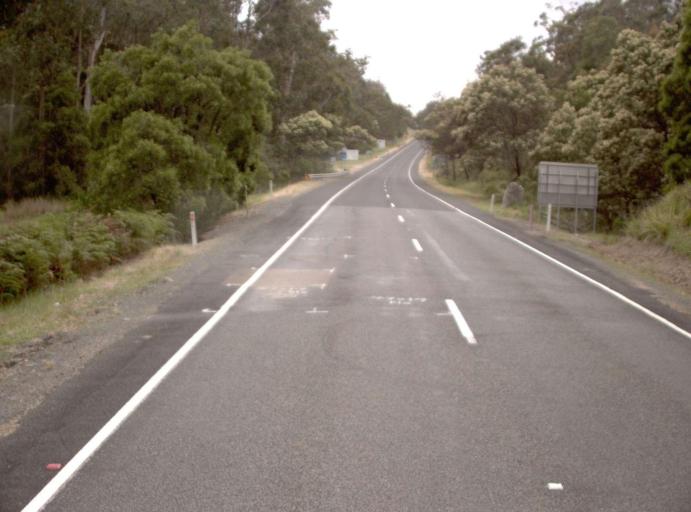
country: AU
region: New South Wales
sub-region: Bombala
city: Bombala
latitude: -37.2314
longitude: 149.2737
